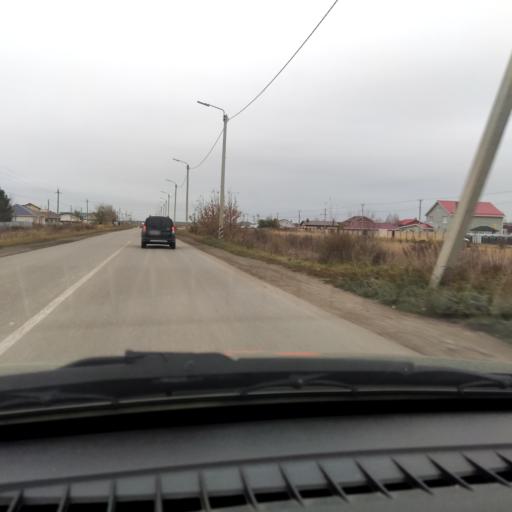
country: RU
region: Samara
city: Podstepki
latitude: 53.5227
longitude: 49.1587
